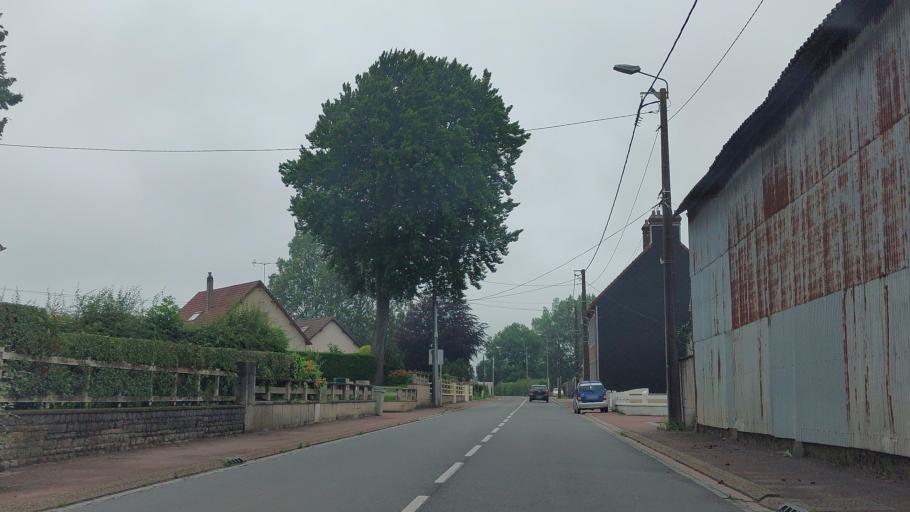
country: FR
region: Picardie
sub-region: Departement de la Somme
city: Bethencourt-sur-Mer
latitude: 50.0790
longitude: 1.4983
